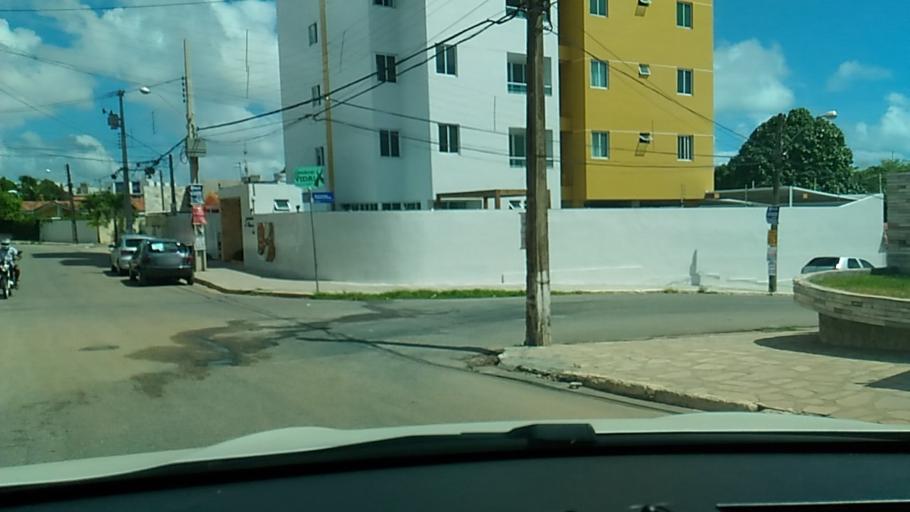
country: BR
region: Paraiba
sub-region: Joao Pessoa
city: Joao Pessoa
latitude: -7.1523
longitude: -34.8453
